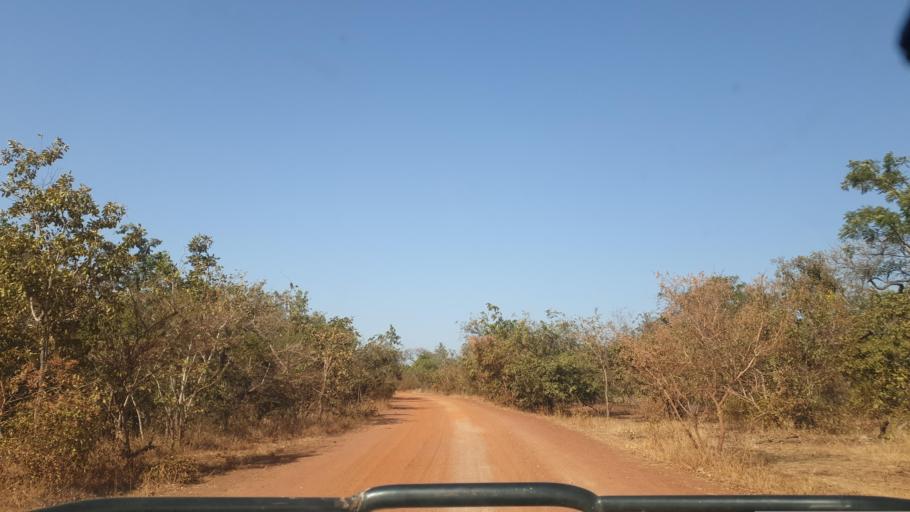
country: ML
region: Sikasso
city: Bougouni
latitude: 11.8206
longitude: -6.9514
